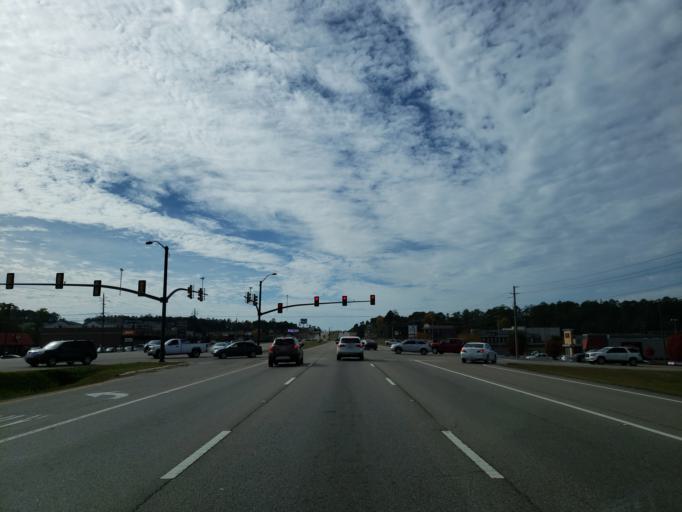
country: US
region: Mississippi
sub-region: Lamar County
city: West Hattiesburg
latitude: 31.3213
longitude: -89.3842
